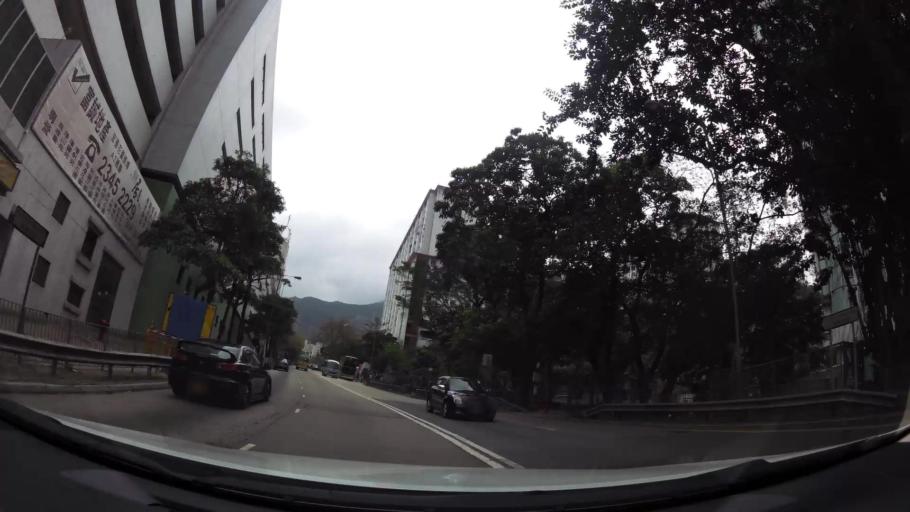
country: HK
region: Wong Tai Sin
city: Wong Tai Sin
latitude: 22.3412
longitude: 114.2085
